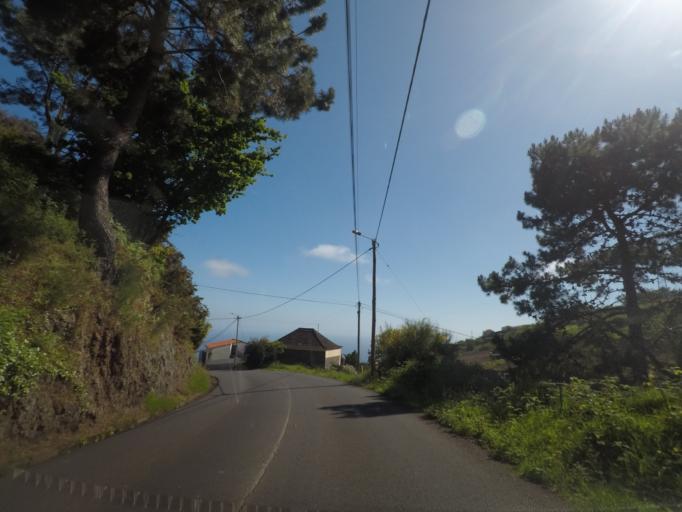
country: PT
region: Madeira
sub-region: Calheta
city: Arco da Calheta
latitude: 32.7069
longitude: -17.1134
